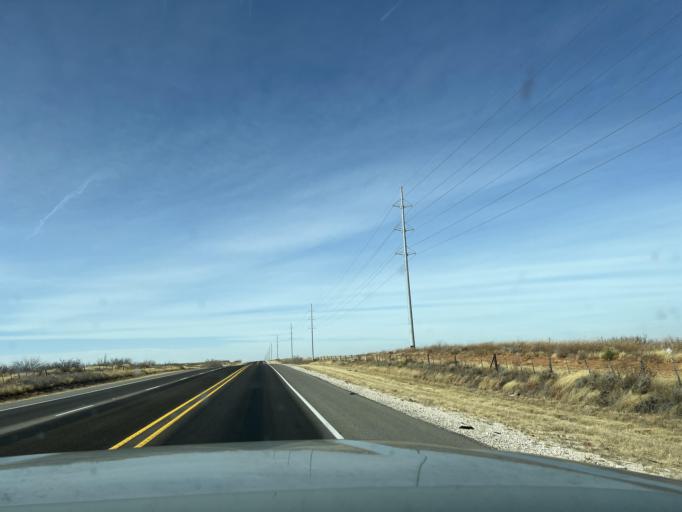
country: US
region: Texas
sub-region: Andrews County
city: Andrews
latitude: 32.3521
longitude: -102.7425
